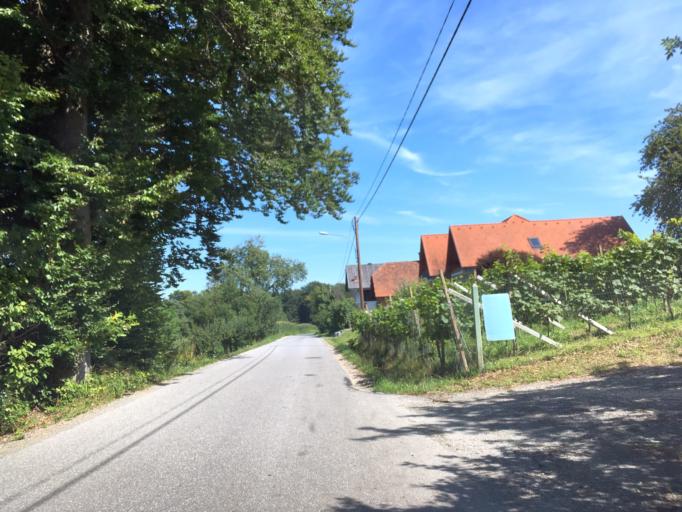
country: AT
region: Styria
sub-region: Politischer Bezirk Leibnitz
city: Sankt Nikolai im Sausal
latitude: 46.8055
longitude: 15.4541
